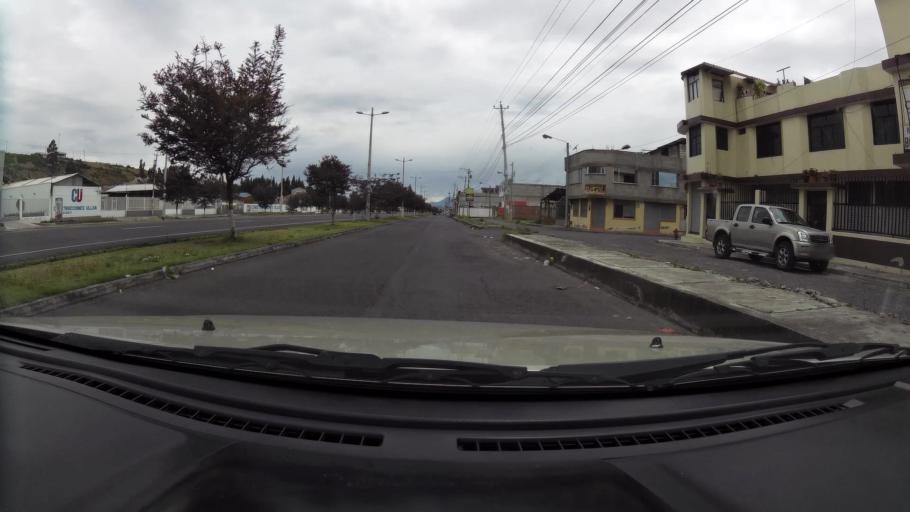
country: EC
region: Cotopaxi
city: Latacunga
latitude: -0.9610
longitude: -78.6097
